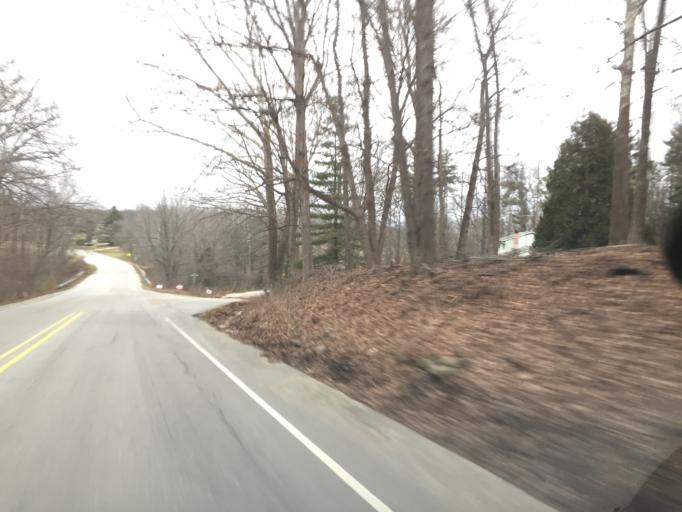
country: US
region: Indiana
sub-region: Monroe County
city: Bloomington
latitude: 39.1994
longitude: -86.5595
